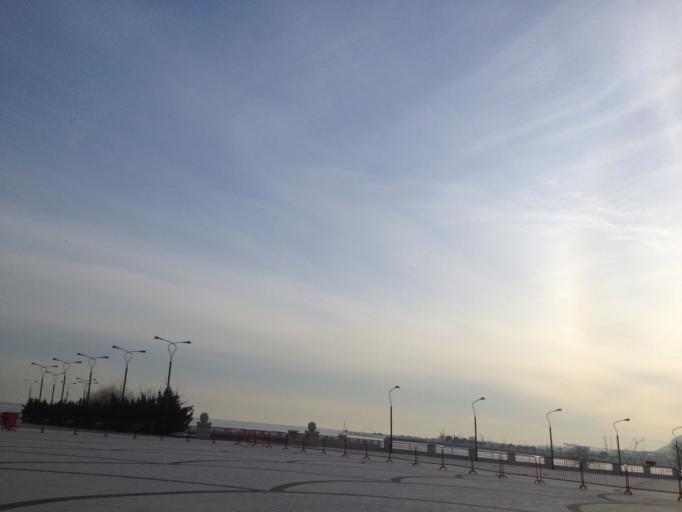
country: AZ
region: Baki
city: Badamdar
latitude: 40.3438
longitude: 49.8466
